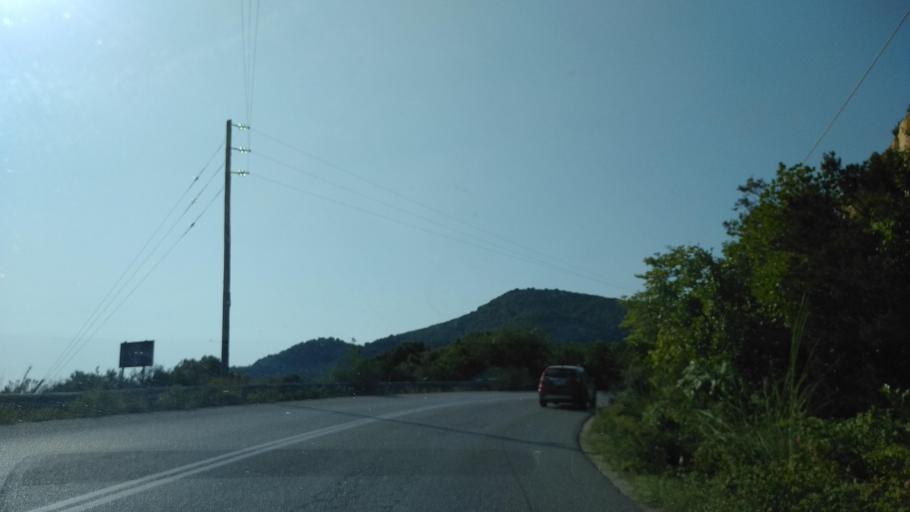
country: GR
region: Central Macedonia
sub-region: Nomos Chalkidikis
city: Stratonion
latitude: 40.5839
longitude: 23.7983
